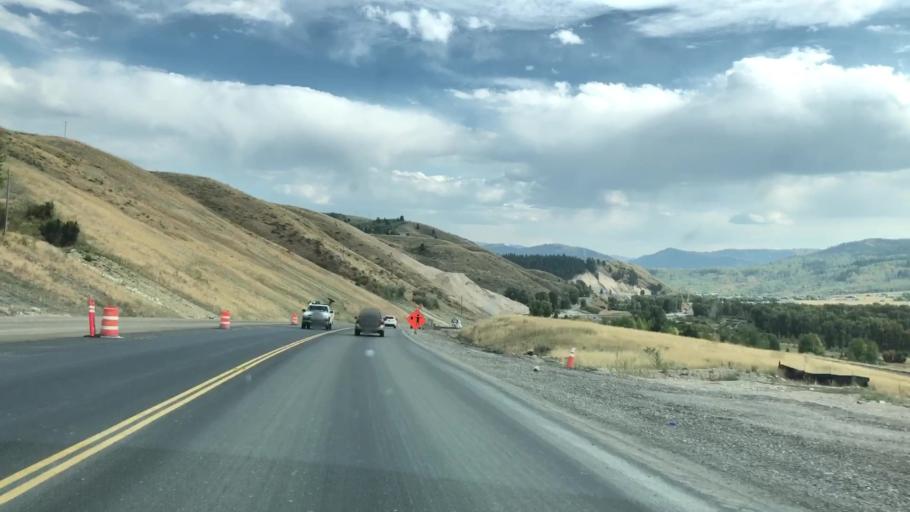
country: US
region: Wyoming
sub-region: Teton County
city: South Park
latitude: 43.3997
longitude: -110.7519
